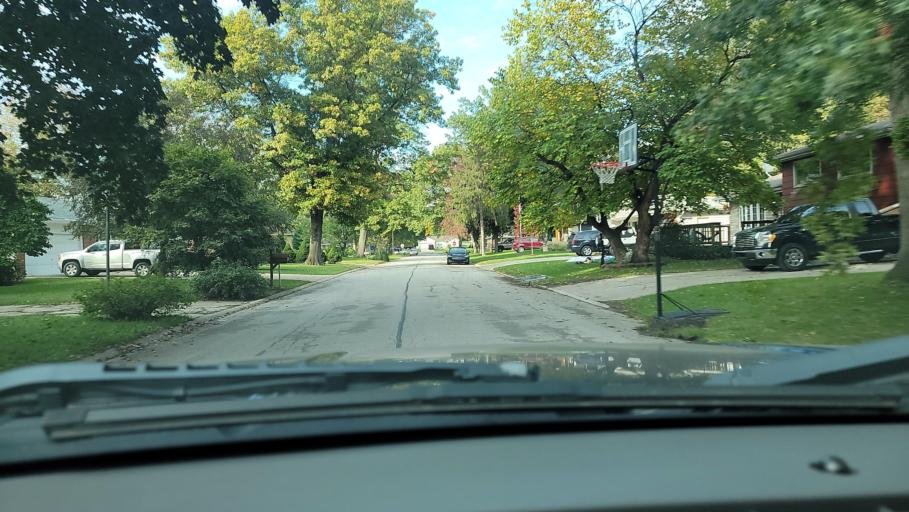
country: US
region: Indiana
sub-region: Porter County
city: Portage
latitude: 41.5829
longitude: -87.1729
